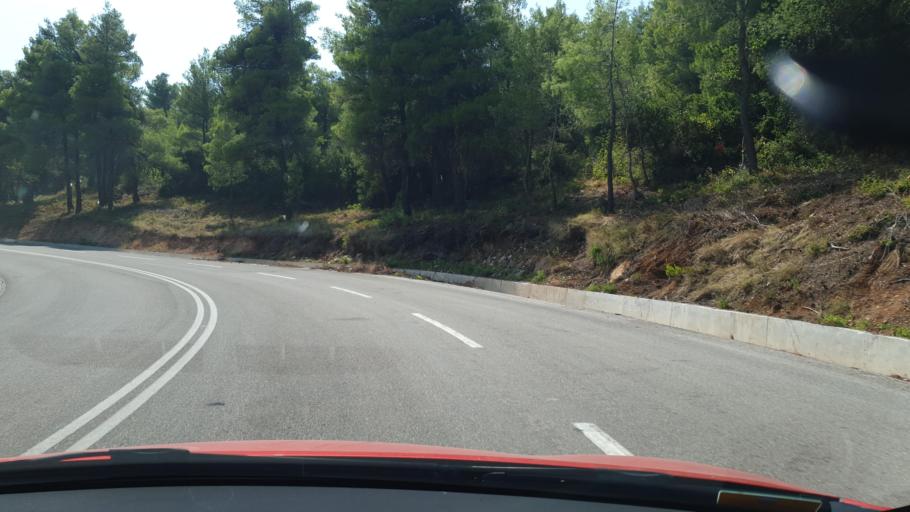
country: GR
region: Central Greece
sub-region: Nomos Evvoias
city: Politika
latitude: 38.6351
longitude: 23.5694
